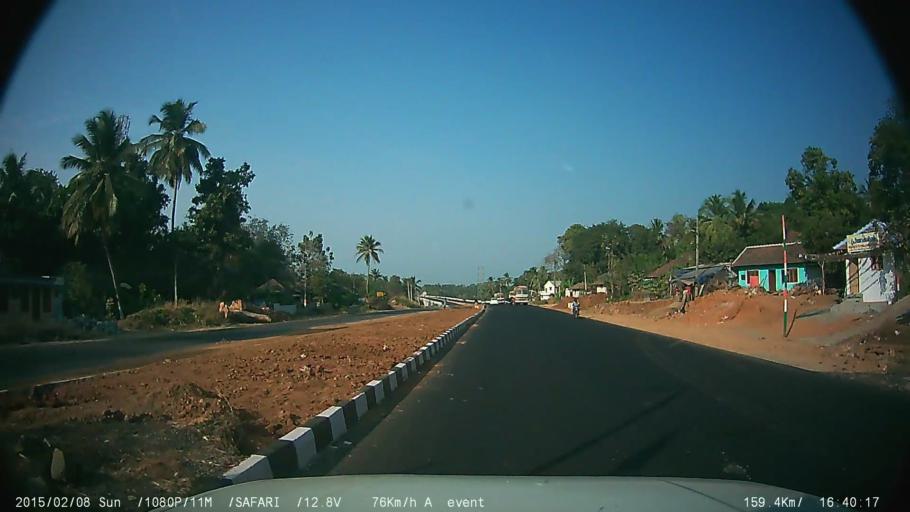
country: IN
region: Kerala
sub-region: Palakkad district
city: Palakkad
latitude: 10.7004
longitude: 76.5914
